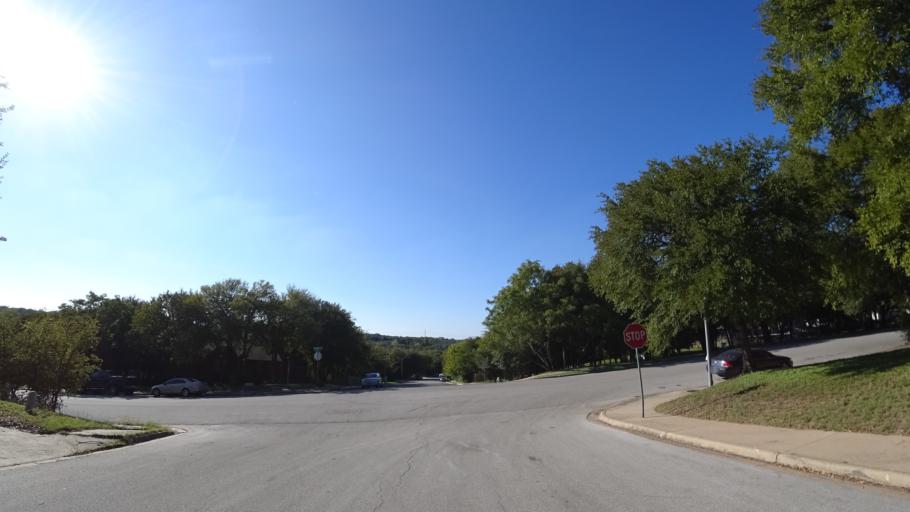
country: US
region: Texas
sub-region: Travis County
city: Austin
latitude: 30.2200
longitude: -97.7262
